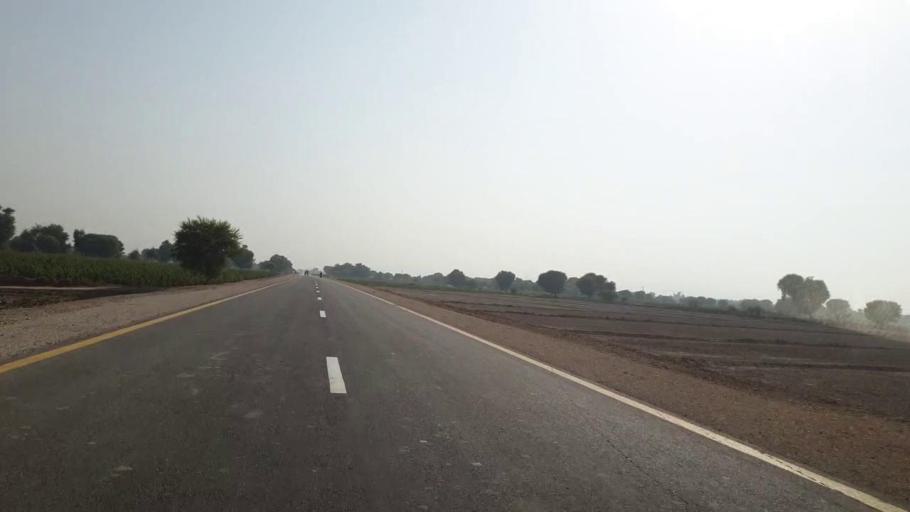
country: PK
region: Sindh
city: Bhan
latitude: 26.5241
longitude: 67.7889
